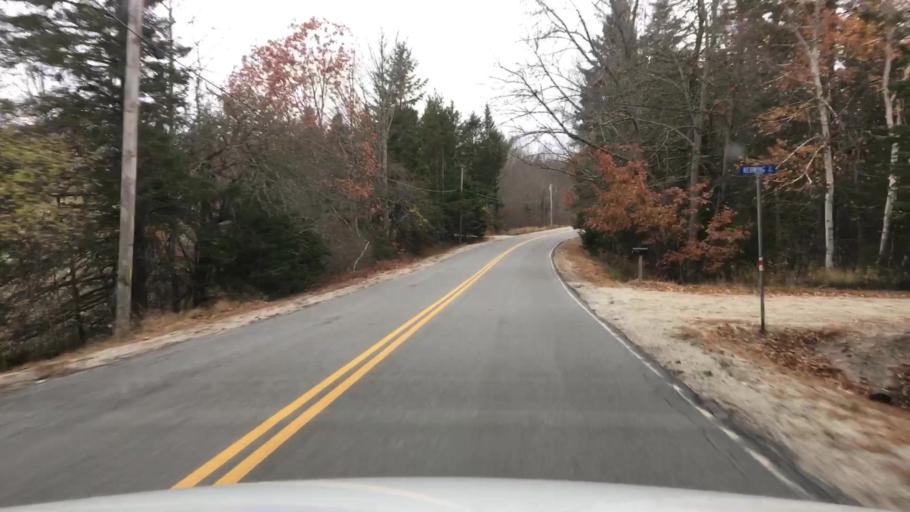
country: US
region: Maine
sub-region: Hancock County
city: Penobscot
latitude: 44.4316
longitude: -68.6289
